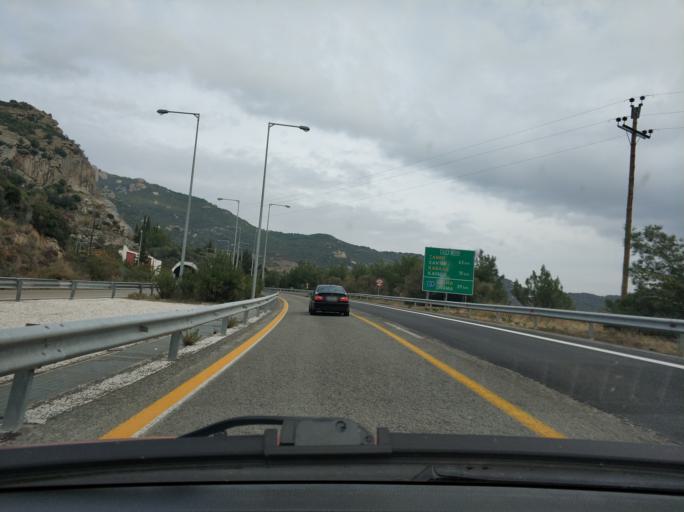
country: GR
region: East Macedonia and Thrace
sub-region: Nomos Kavalas
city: Palaio Tsifliki
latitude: 40.9040
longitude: 24.3404
